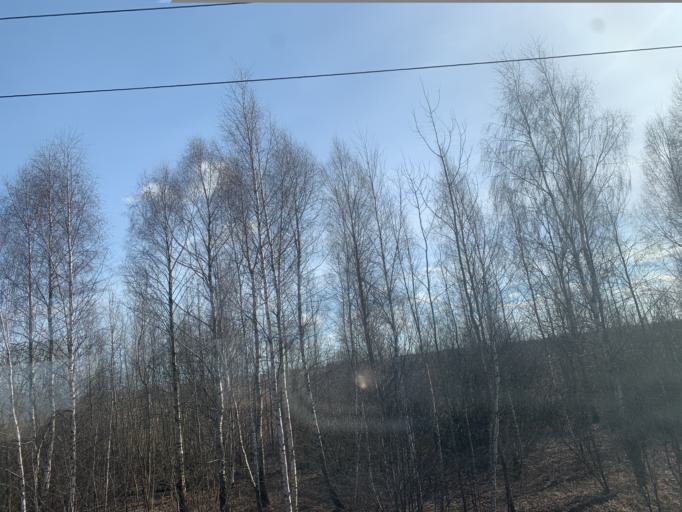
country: BY
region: Minsk
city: Stan'kava
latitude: 53.6893
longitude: 27.2282
